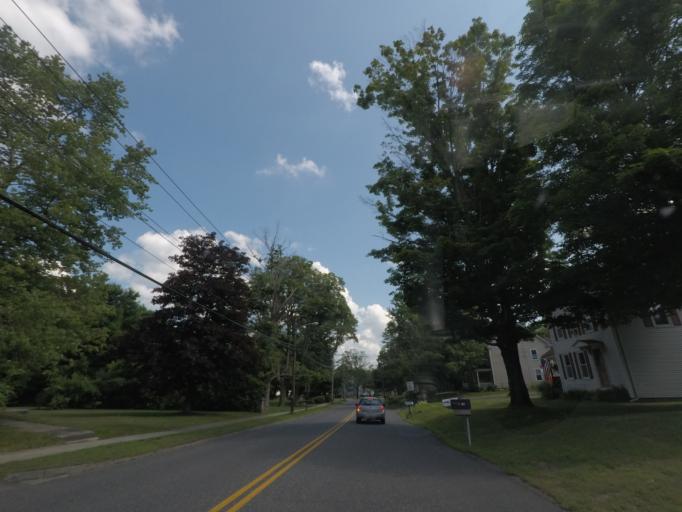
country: US
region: Massachusetts
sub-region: Hampden County
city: Monson
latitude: 42.1110
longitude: -72.3255
